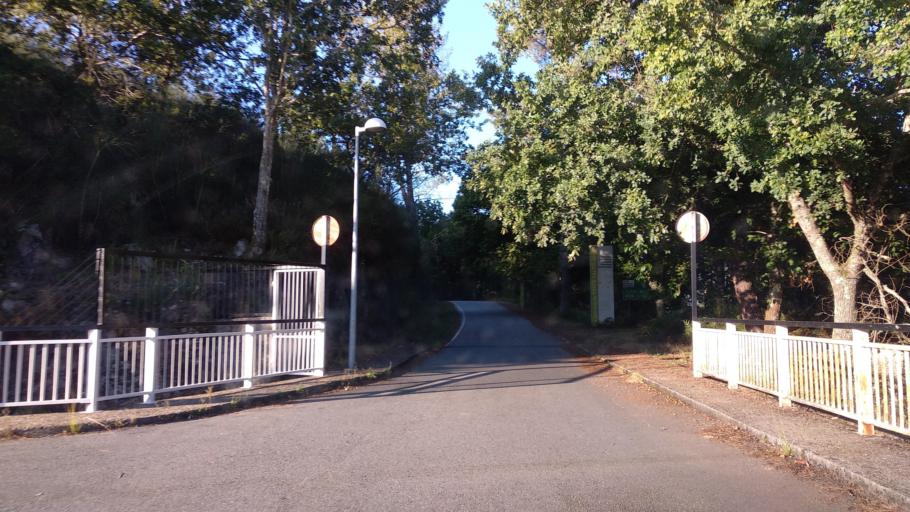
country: ES
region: Galicia
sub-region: Provincia de Pontevedra
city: Fornelos de Montes
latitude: 42.3471
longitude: -8.4896
